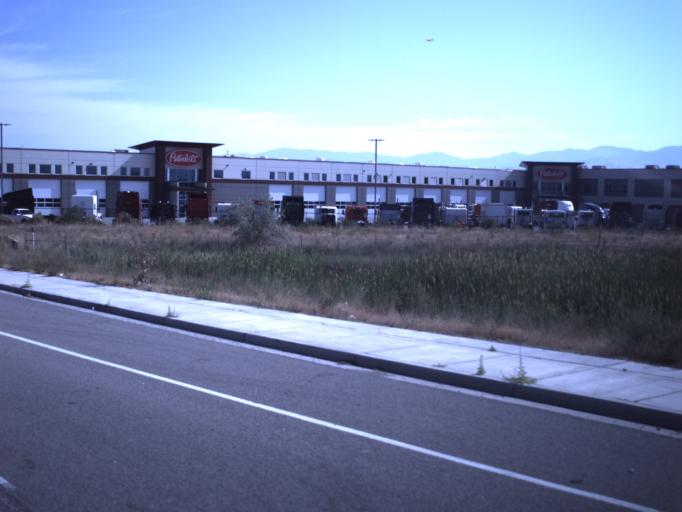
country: US
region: Utah
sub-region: Salt Lake County
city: West Valley City
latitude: 40.7279
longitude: -112.0248
